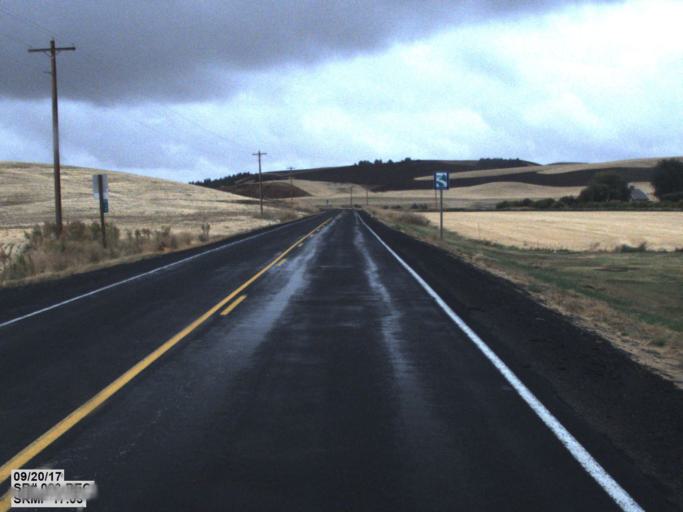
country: US
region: Washington
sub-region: Whitman County
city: Colfax
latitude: 47.1087
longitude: -117.6349
